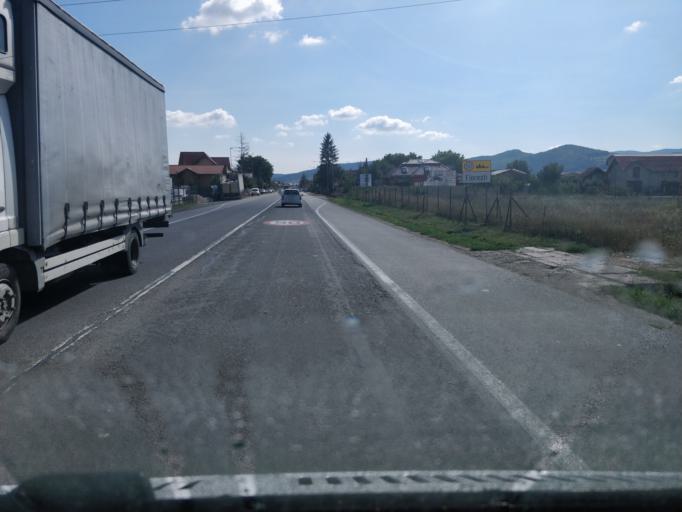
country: RO
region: Cluj
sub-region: Comuna Floresti
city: Luna de Sus
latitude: 46.7442
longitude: 23.4624
